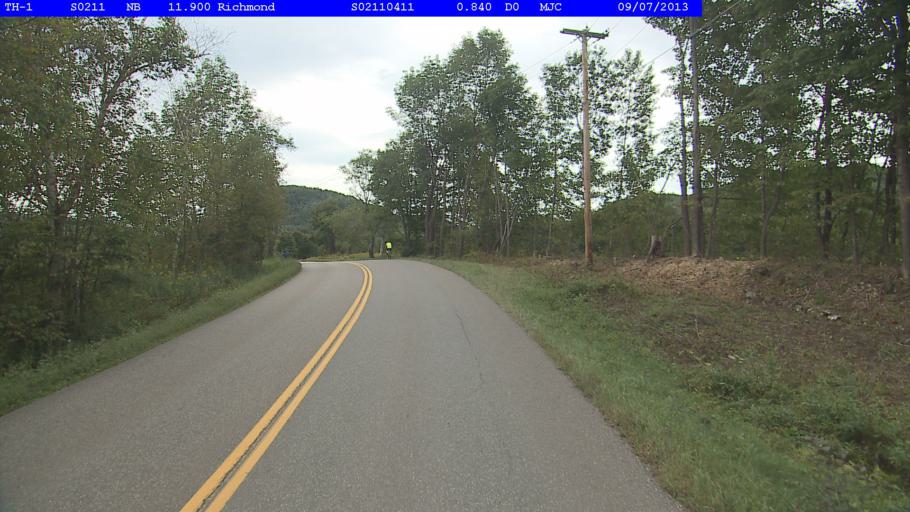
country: US
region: Vermont
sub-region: Chittenden County
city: Williston
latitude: 44.3648
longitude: -72.9959
